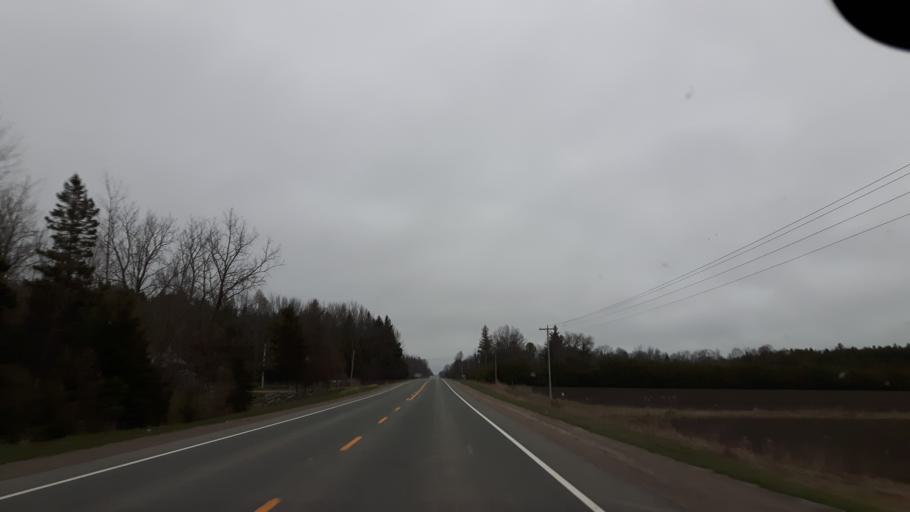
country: CA
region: Ontario
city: Goderich
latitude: 43.6715
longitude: -81.7057
